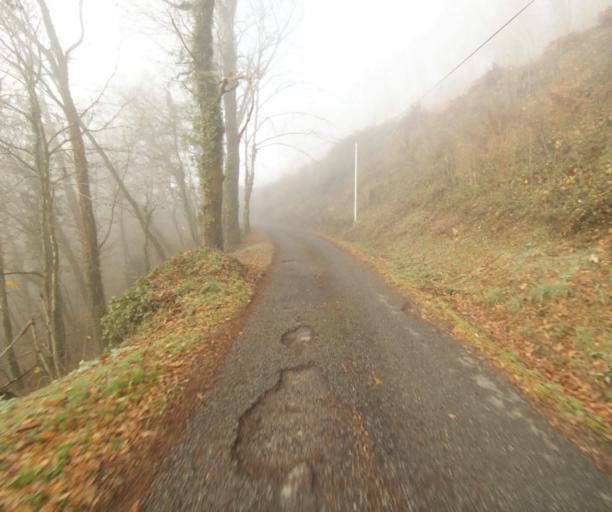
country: FR
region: Limousin
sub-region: Departement de la Correze
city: Tulle
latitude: 45.2619
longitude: 1.7844
